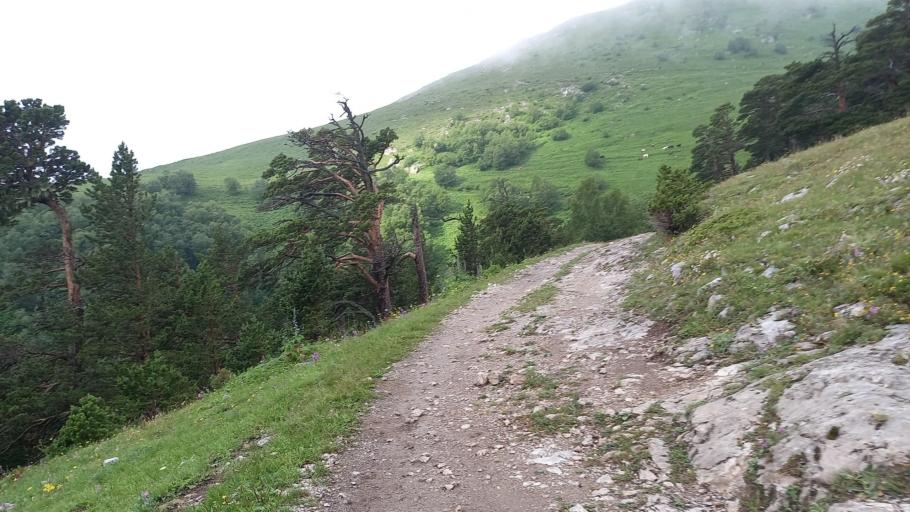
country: RU
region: Karachayevo-Cherkesiya
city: Kurdzhinovo
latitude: 43.7928
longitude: 40.8371
